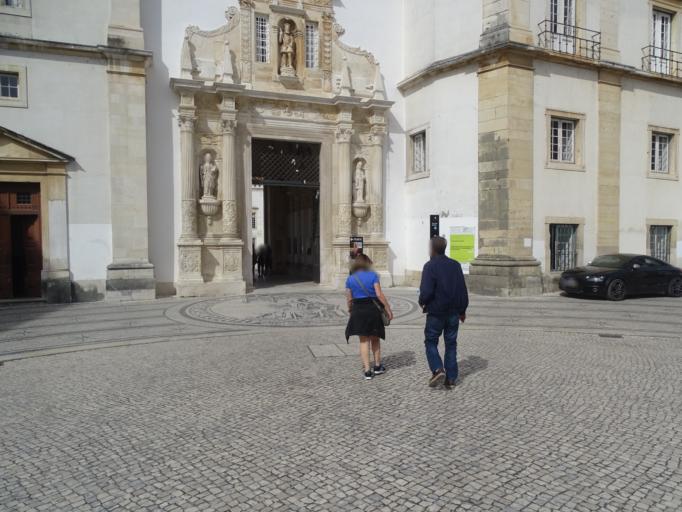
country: PT
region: Coimbra
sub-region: Coimbra
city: Coimbra
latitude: 40.2079
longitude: -8.4254
